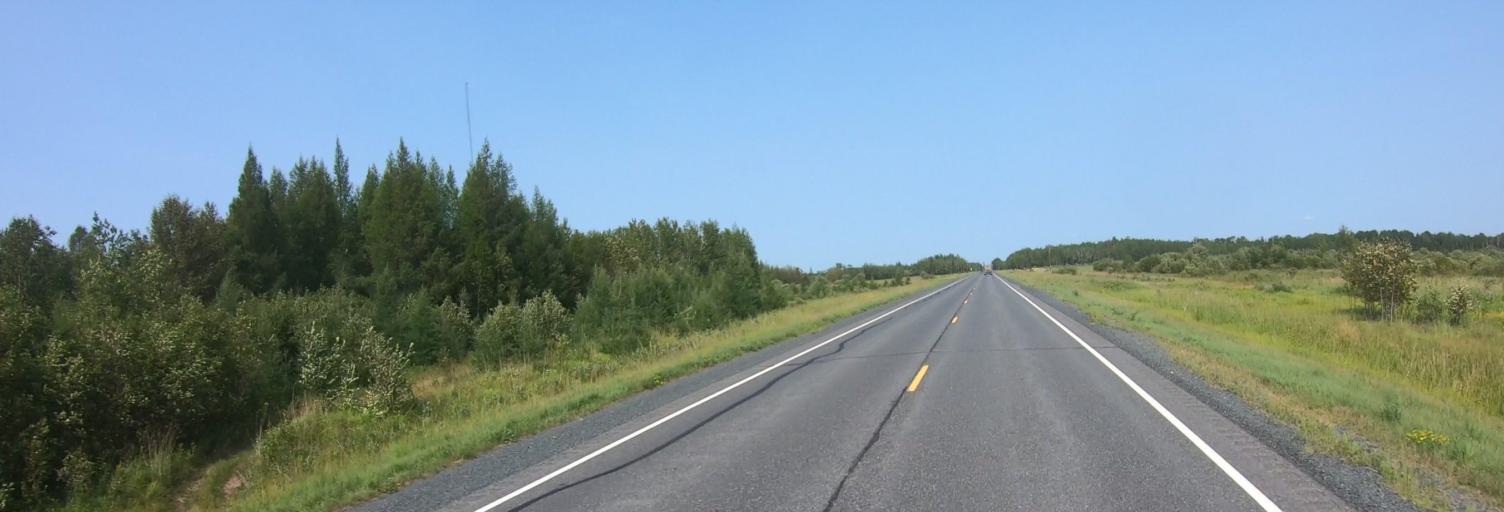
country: US
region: Minnesota
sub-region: Koochiching County
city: International Falls
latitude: 48.5576
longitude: -93.8182
